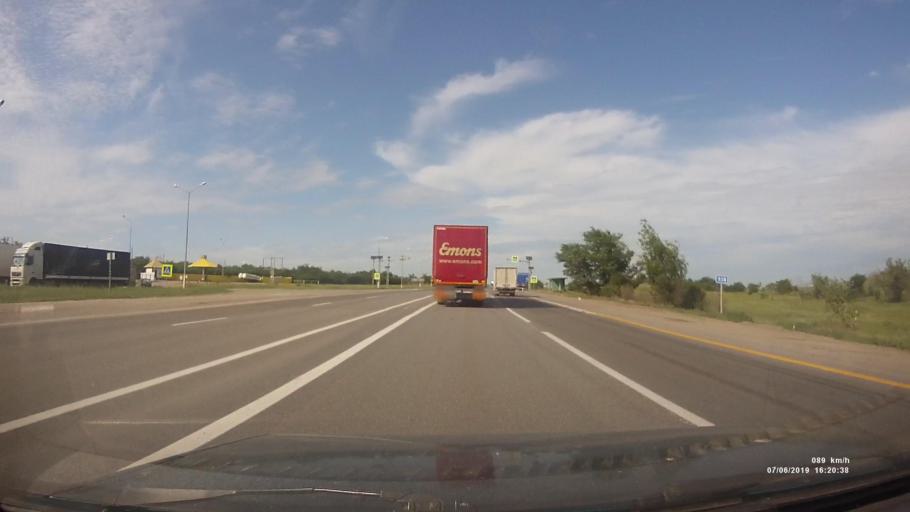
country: RU
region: Rostov
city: Kamensk-Shakhtinskiy
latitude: 48.2445
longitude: 40.2854
